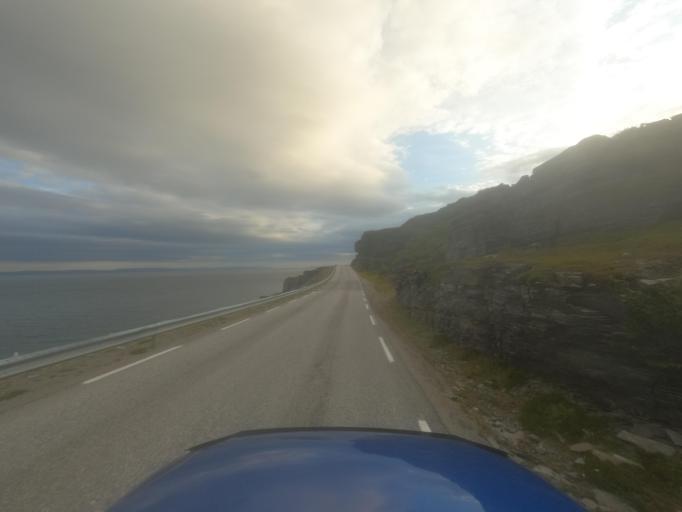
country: NO
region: Finnmark Fylke
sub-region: Nordkapp
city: Honningsvag
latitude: 70.6842
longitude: 25.4888
